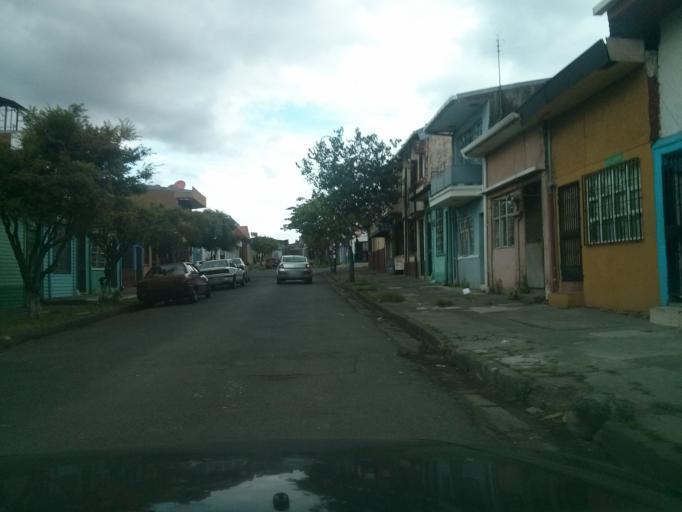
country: CR
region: San Jose
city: San Jose
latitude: 9.9275
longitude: -84.0823
